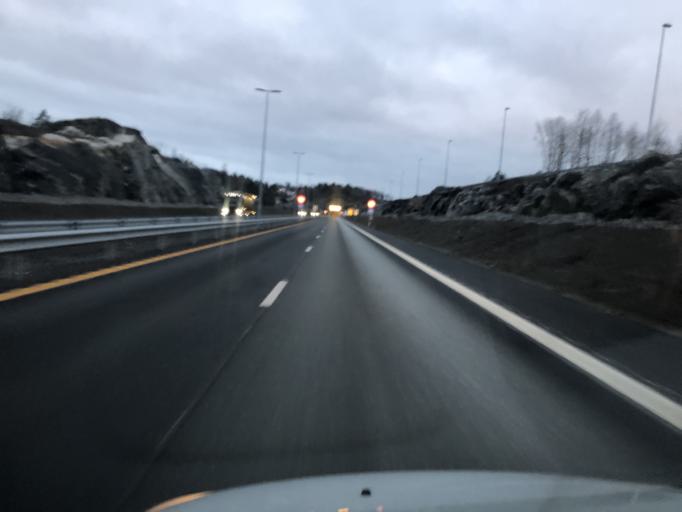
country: NO
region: Aust-Agder
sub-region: Arendal
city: Arendal
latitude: 58.4882
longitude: 8.7628
